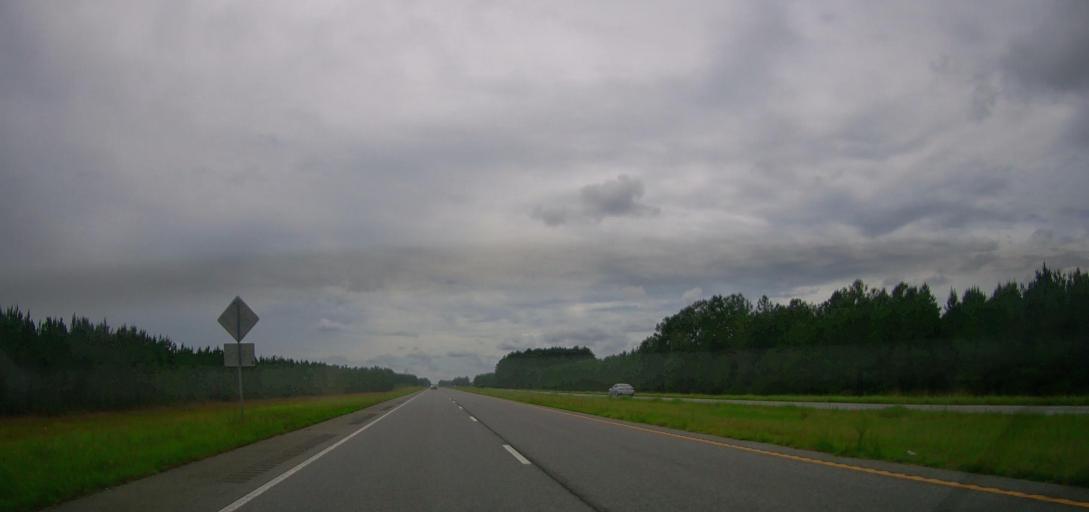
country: US
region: Georgia
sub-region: Appling County
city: Baxley
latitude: 31.7512
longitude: -82.2697
